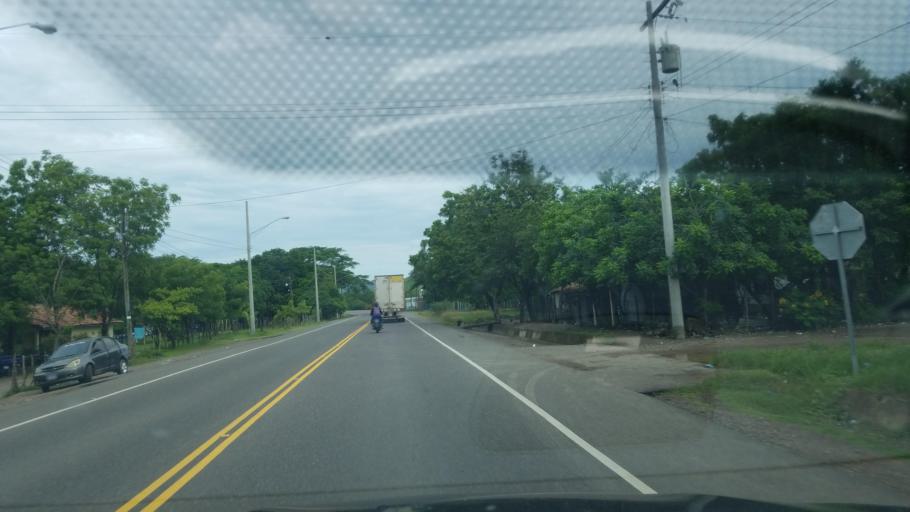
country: HN
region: Valle
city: Goascoran
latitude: 13.5390
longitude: -87.6037
